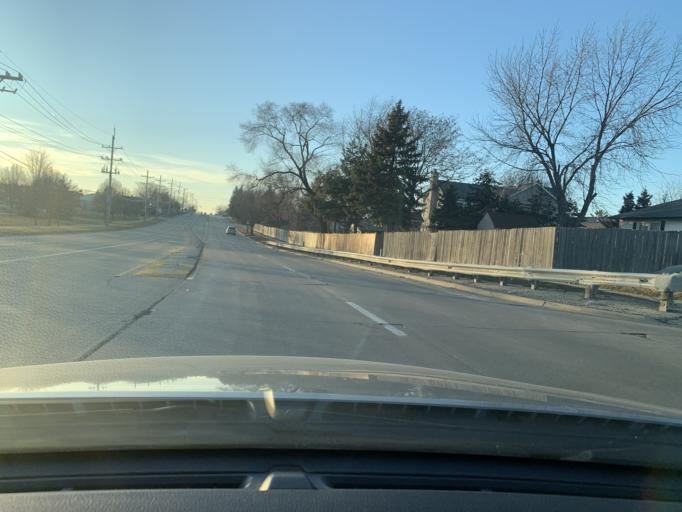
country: US
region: Illinois
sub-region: DuPage County
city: Itasca
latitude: 41.9995
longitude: -88.0393
